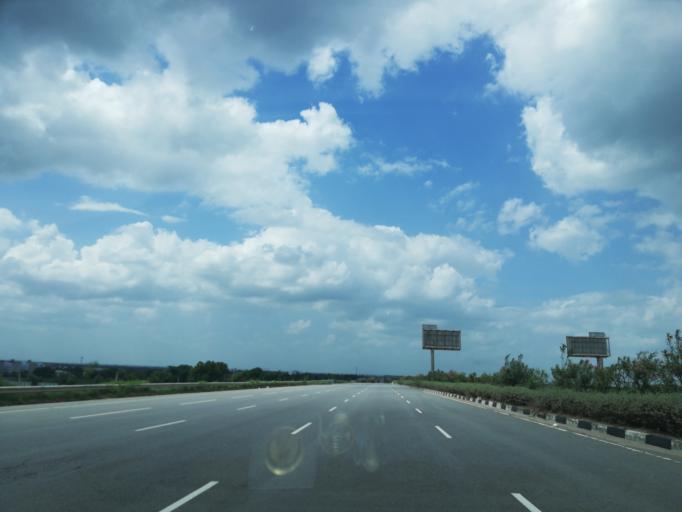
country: IN
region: Telangana
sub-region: Medak
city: Serilingampalle
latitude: 17.4702
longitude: 78.2484
